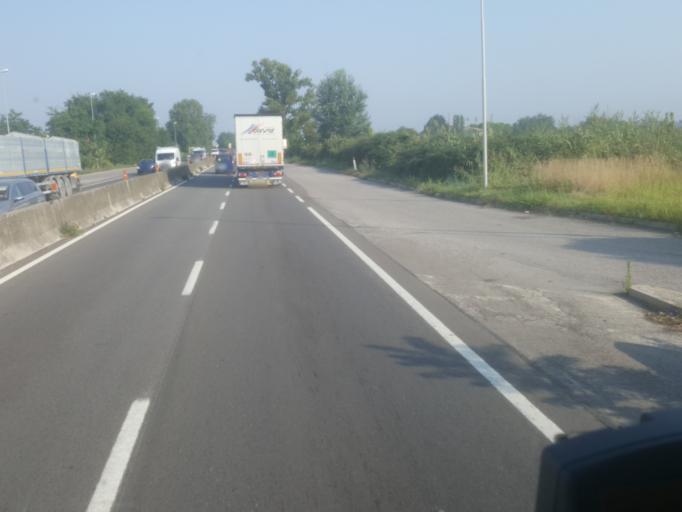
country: IT
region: Emilia-Romagna
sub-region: Provincia di Ravenna
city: Ravenna
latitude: 44.4151
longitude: 12.1696
